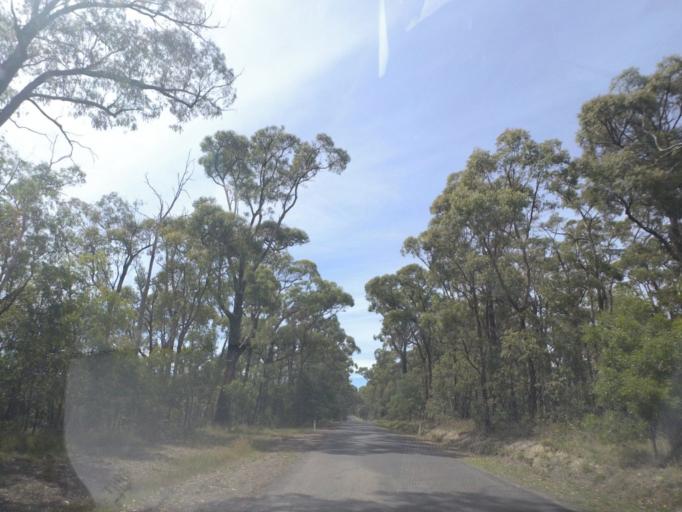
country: AU
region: Victoria
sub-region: Yarra Ranges
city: Yarra Glen
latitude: -37.5269
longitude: 145.4351
